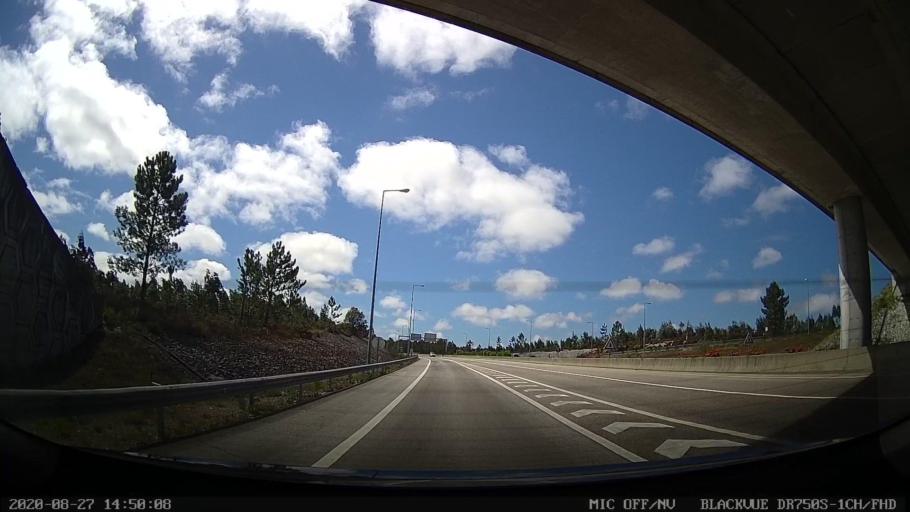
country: PT
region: Leiria
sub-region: Leiria
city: Maceira
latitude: 39.7427
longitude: -8.8717
